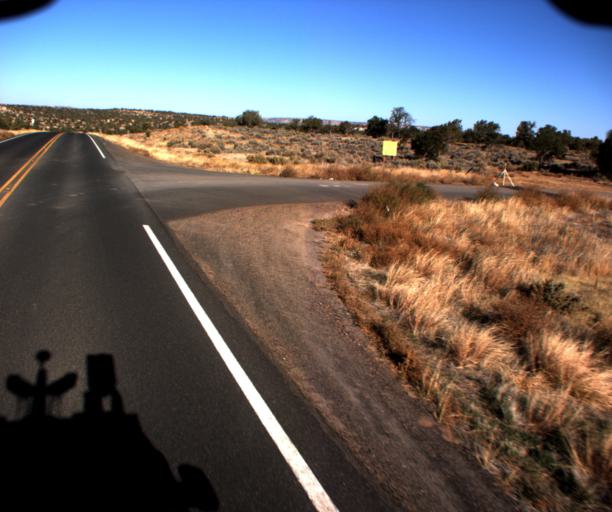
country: US
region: Arizona
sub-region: Apache County
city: Ganado
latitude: 35.7656
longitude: -109.7896
